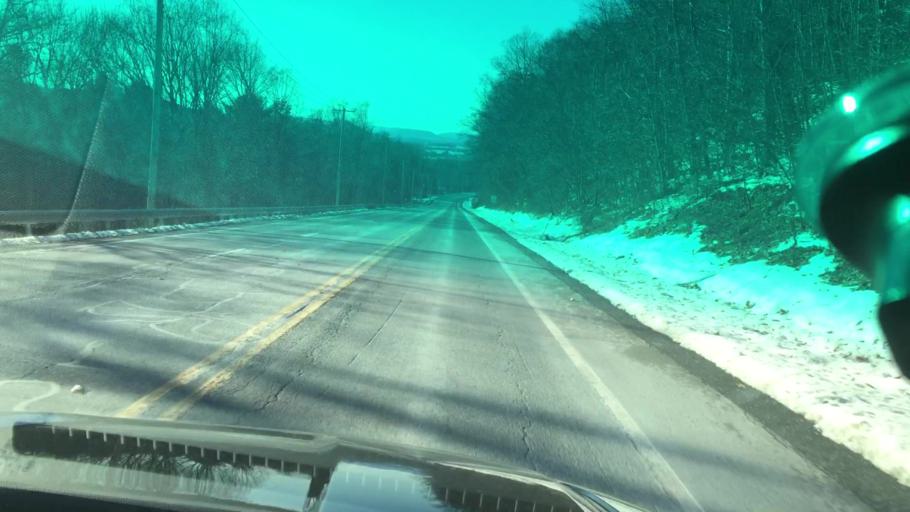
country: US
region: Pennsylvania
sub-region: Luzerne County
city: Oakdale
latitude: 41.0184
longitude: -75.9426
